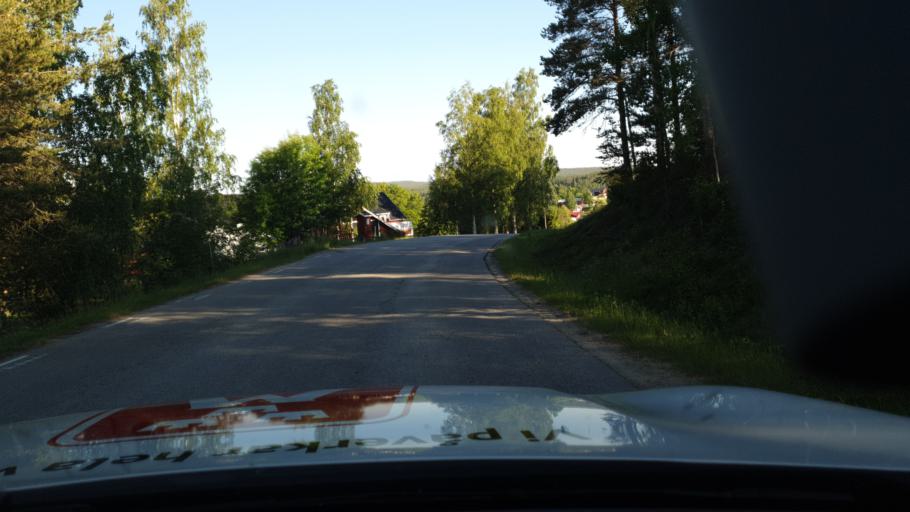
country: SE
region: Vaesterbotten
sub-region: Umea Kommun
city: Roback
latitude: 64.0335
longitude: 20.0812
